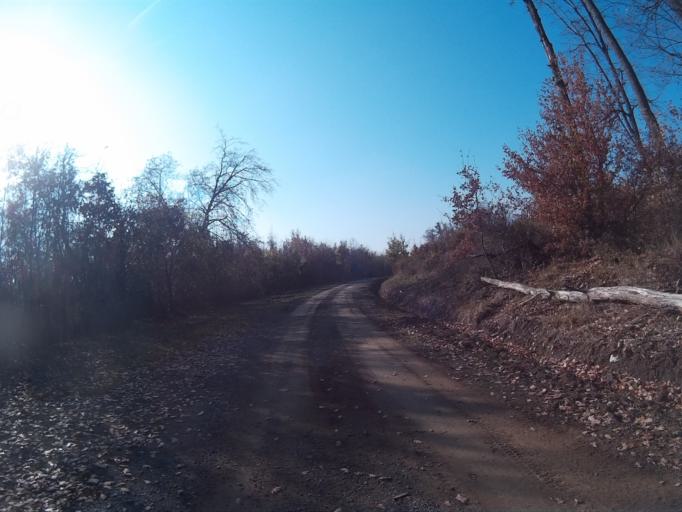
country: HU
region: Heves
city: Felsotarkany
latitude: 48.0108
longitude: 20.4002
